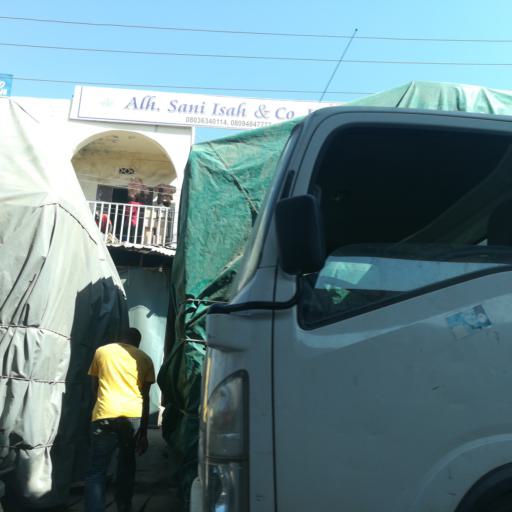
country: NG
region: Kano
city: Kano
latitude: 12.0105
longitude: 8.5374
